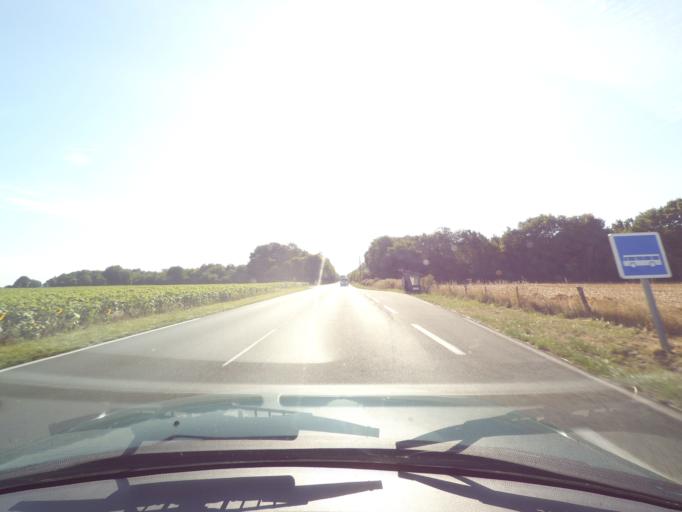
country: FR
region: Poitou-Charentes
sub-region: Departement de la Vienne
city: Ayron
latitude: 46.6609
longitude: 0.0176
